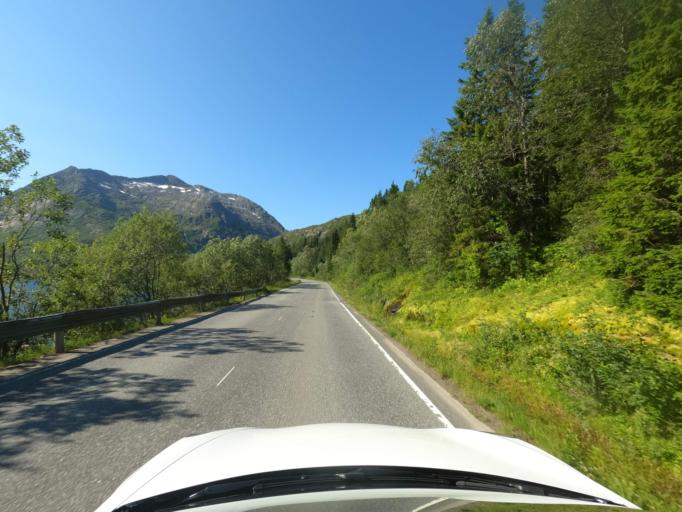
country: NO
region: Nordland
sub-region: Lodingen
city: Lodingen
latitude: 68.5436
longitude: 15.7347
